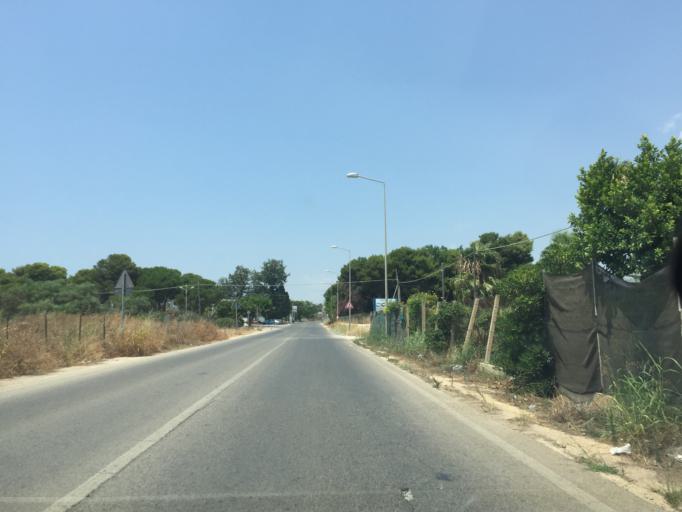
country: IT
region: Sicily
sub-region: Ragusa
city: Donnalucata
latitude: 36.7707
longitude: 14.6108
